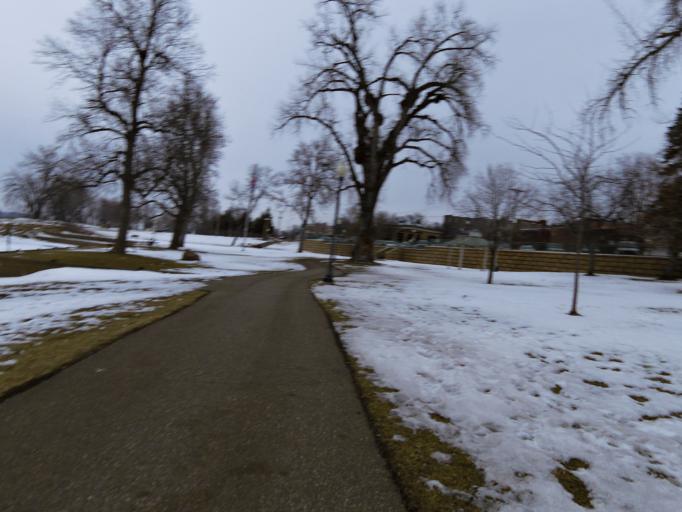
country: US
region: Wisconsin
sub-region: Saint Croix County
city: Hudson
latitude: 44.9736
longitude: -92.7587
